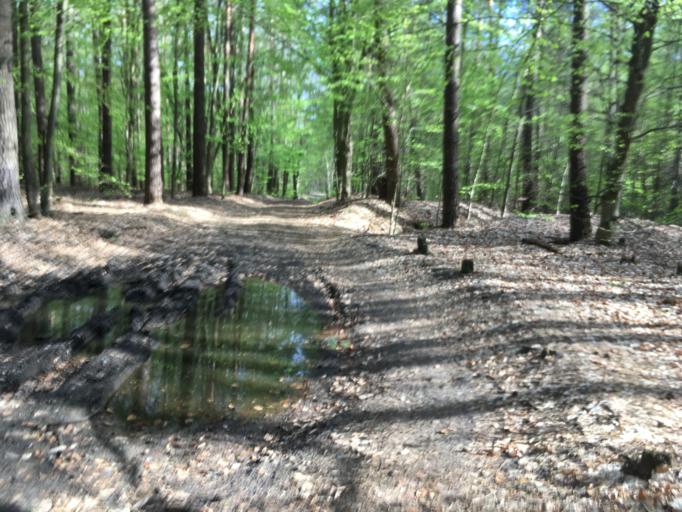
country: DE
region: Brandenburg
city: Bernau bei Berlin
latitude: 52.7178
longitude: 13.5638
